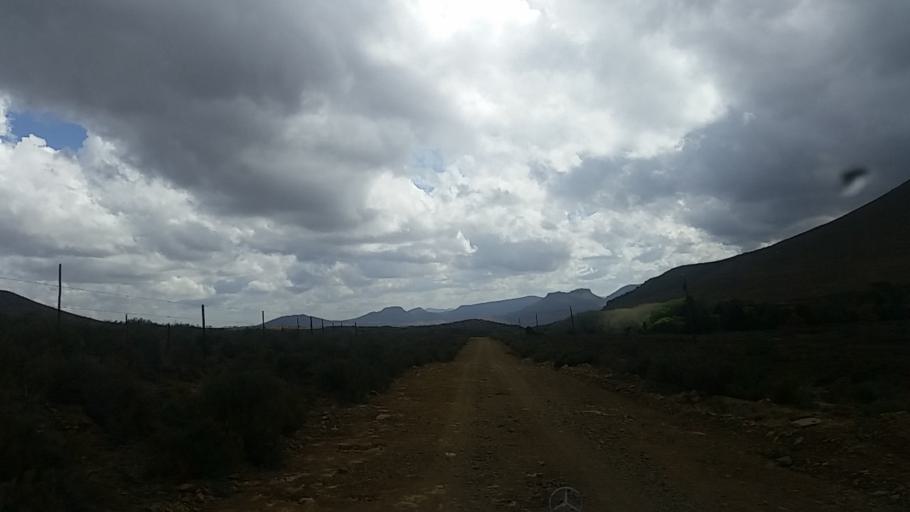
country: ZA
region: Eastern Cape
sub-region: Chris Hani District Municipality
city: Middelburg
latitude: -31.7901
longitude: 24.6673
